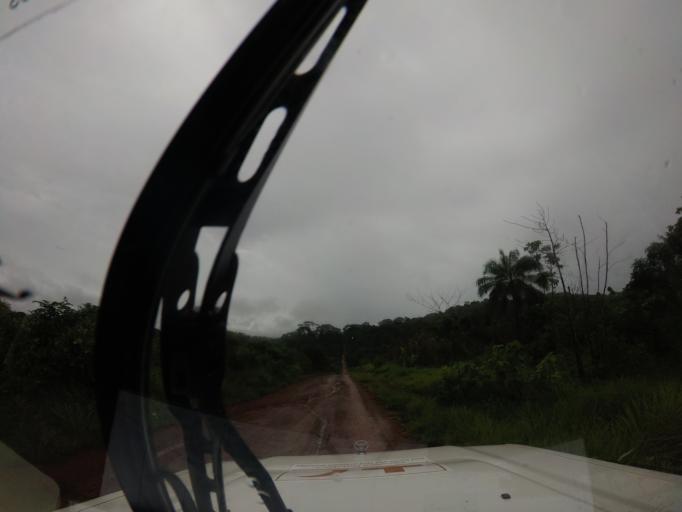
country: SL
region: Eastern Province
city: Kenema
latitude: 7.7294
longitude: -11.1887
